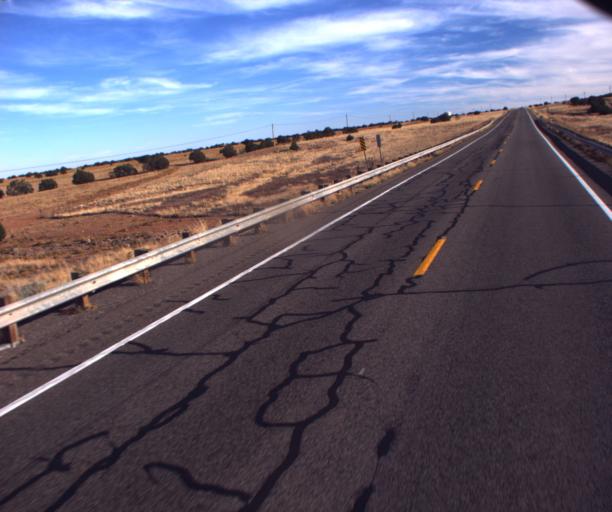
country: US
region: New Mexico
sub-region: San Juan County
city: Shiprock
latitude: 36.9053
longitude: -109.0698
